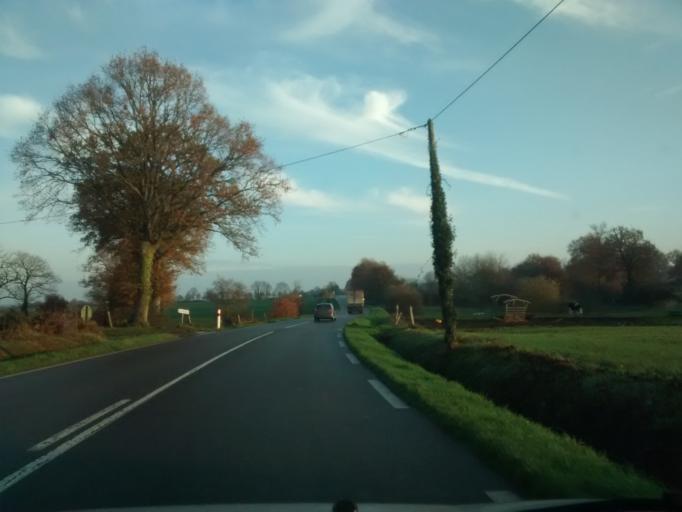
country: FR
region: Brittany
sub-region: Departement d'Ille-et-Vilaine
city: Tremblay
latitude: 48.3855
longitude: -1.4915
